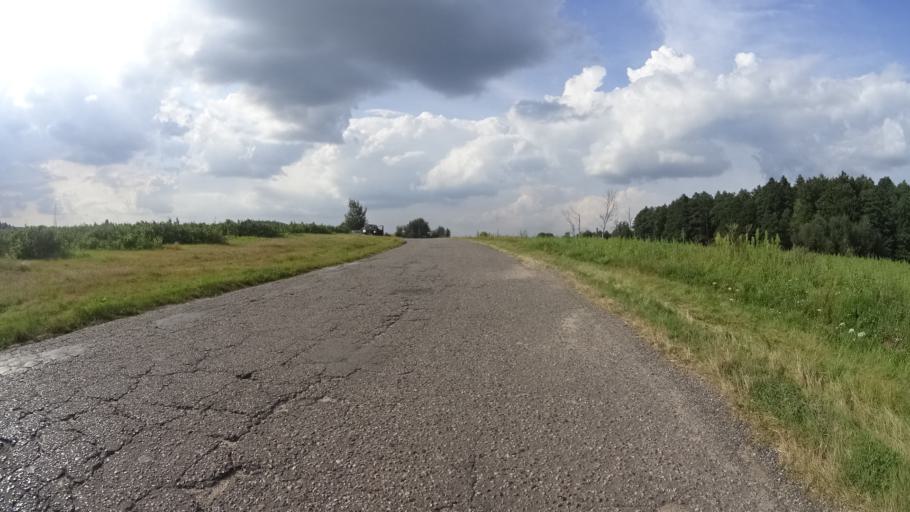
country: PL
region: Masovian Voivodeship
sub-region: Powiat grojecki
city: Mogielnica
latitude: 51.6643
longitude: 20.7448
